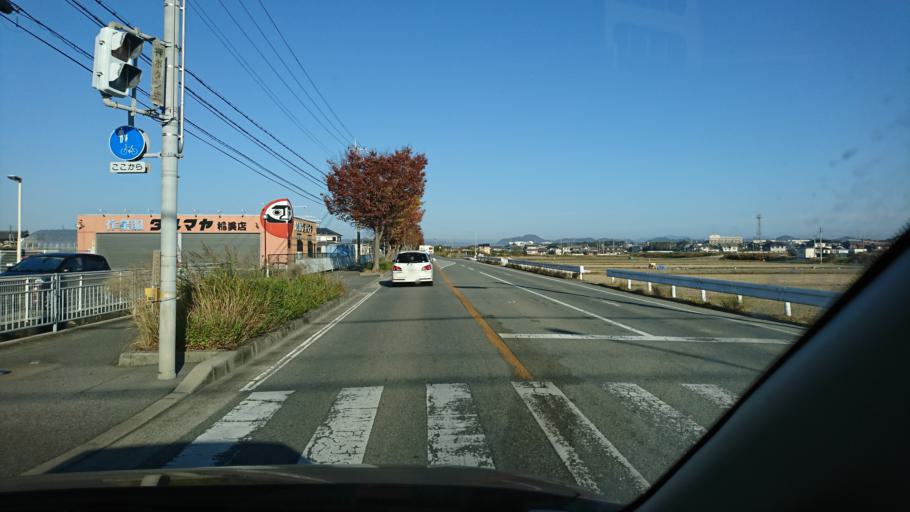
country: JP
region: Hyogo
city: Kakogawacho-honmachi
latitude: 34.7535
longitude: 134.8925
